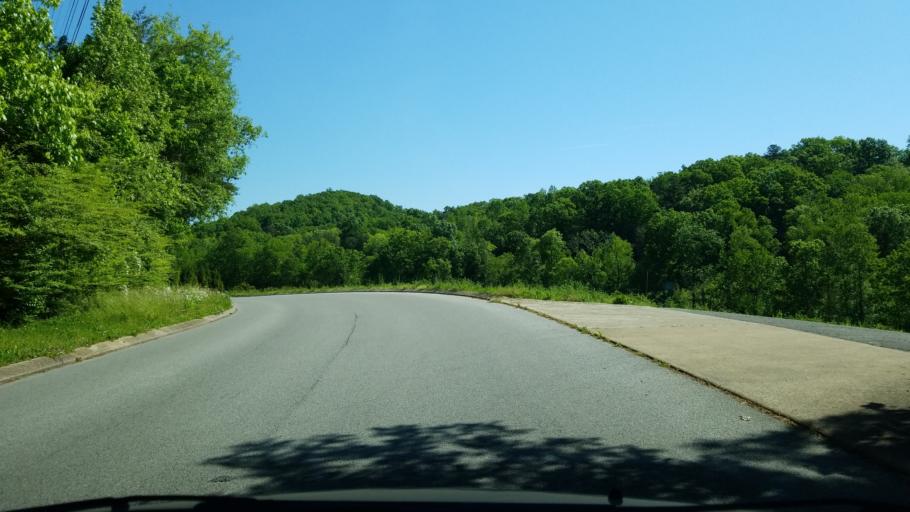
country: US
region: Tennessee
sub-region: Hamilton County
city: Walden
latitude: 35.1451
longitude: -85.2998
